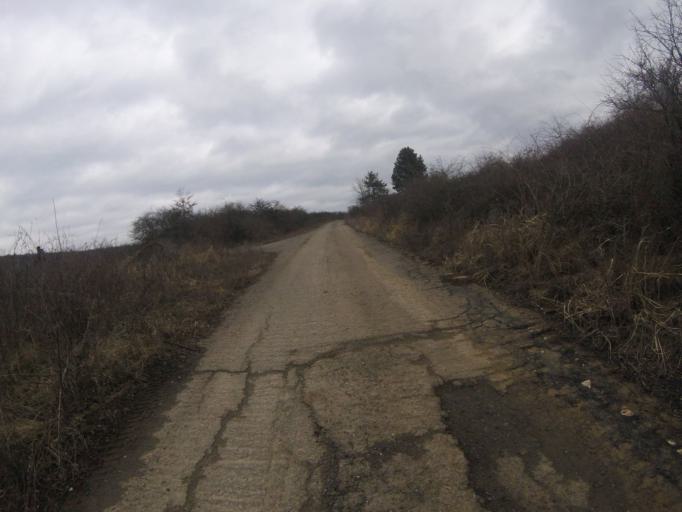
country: HU
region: Heves
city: Egerszalok
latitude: 47.8473
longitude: 20.3436
